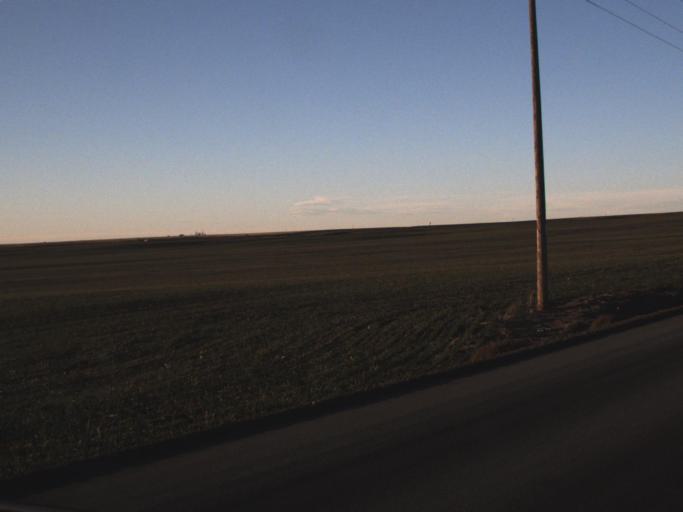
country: US
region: Washington
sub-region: Franklin County
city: Connell
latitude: 46.7886
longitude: -118.5473
